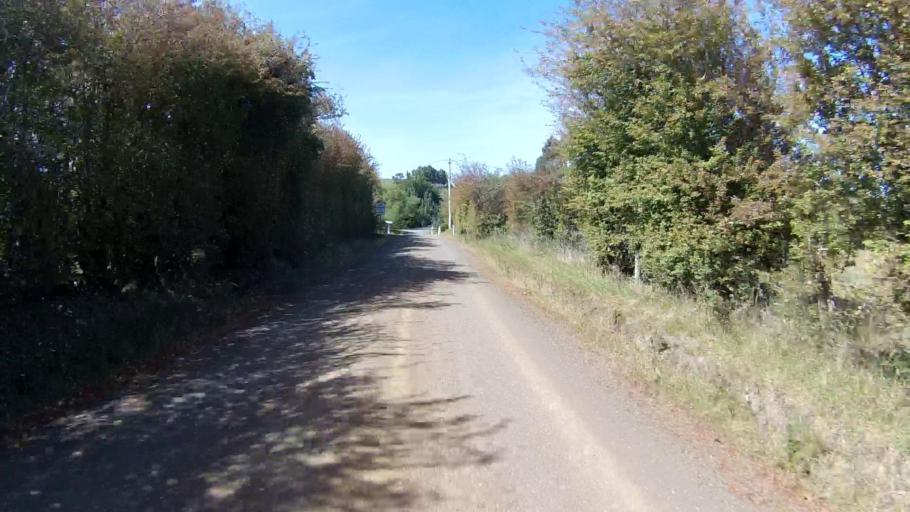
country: AU
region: Tasmania
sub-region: Sorell
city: Sorell
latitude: -42.7517
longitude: 147.6261
